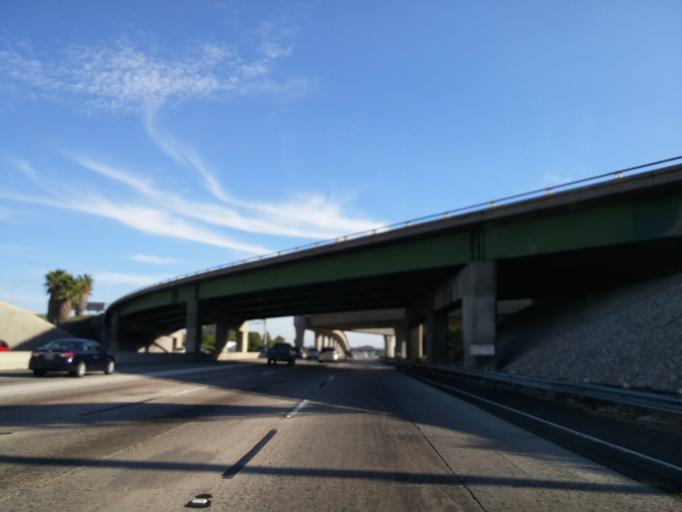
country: US
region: California
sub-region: Orange County
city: Laguna Woods
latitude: 33.6452
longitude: -117.7358
